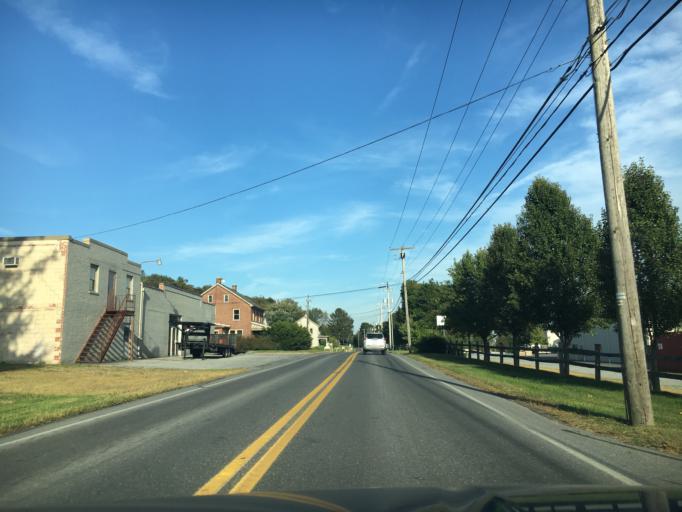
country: US
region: Pennsylvania
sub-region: Lancaster County
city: Akron
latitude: 40.1298
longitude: -76.1558
